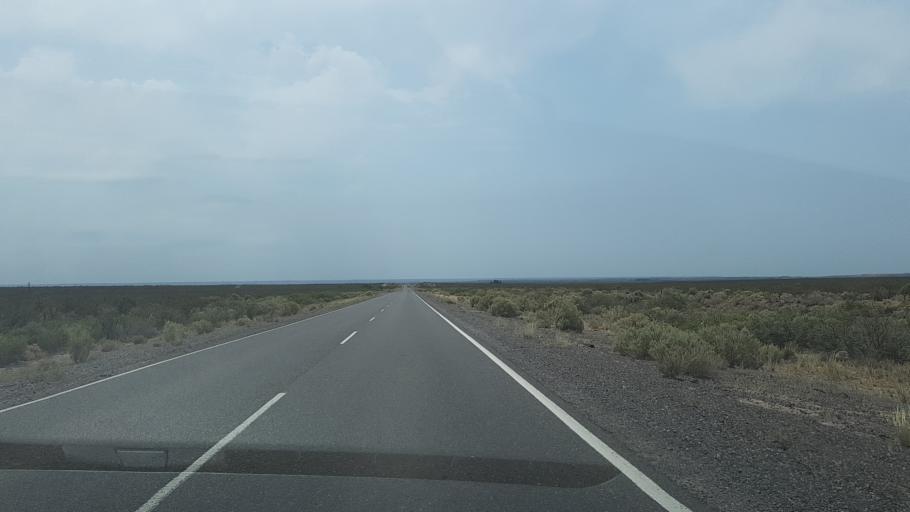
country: AR
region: Rio Negro
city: Catriel
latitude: -38.0741
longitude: -67.9236
